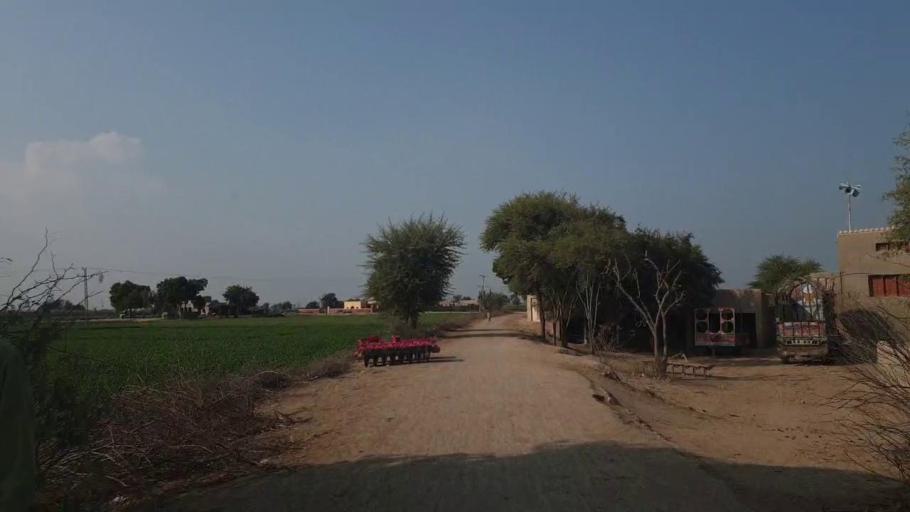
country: PK
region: Sindh
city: Hala
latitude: 25.8315
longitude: 68.3998
